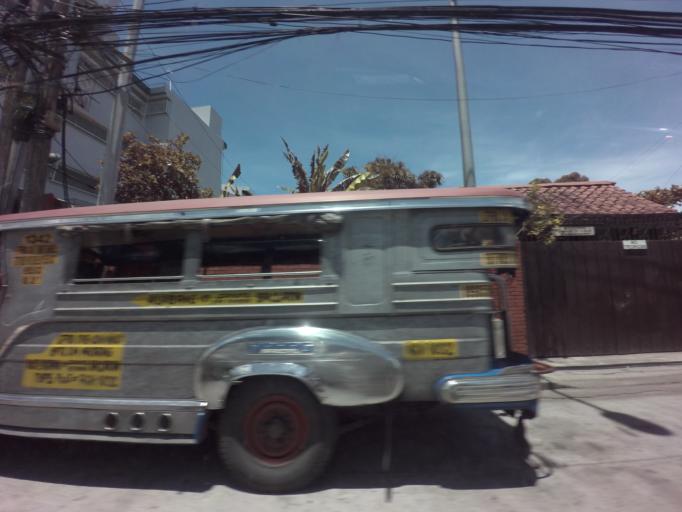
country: PH
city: Sambayanihan People's Village
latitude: 14.4858
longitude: 120.9852
